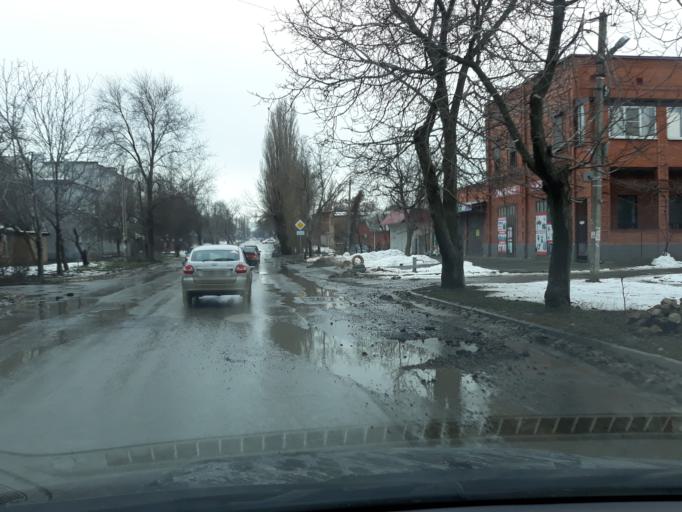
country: RU
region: Rostov
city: Taganrog
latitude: 47.2245
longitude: 38.9039
